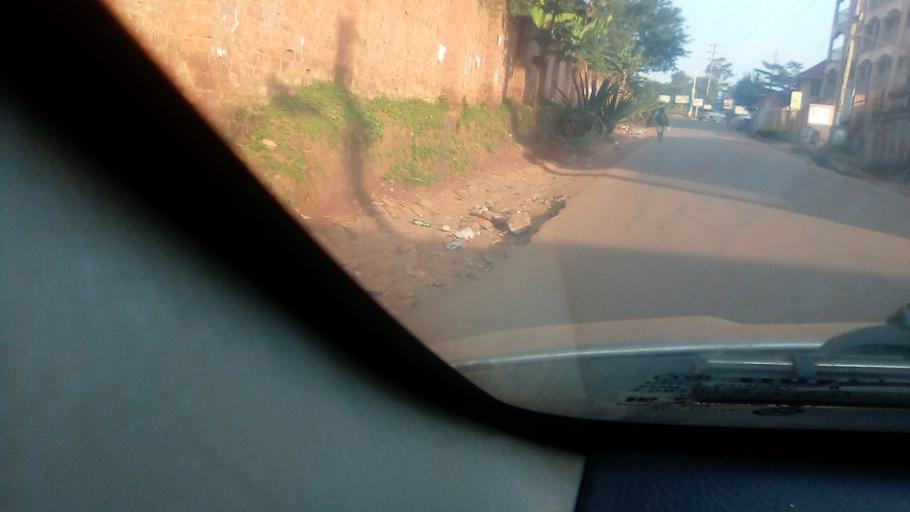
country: UG
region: Central Region
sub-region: Wakiso District
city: Kireka
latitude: 0.3449
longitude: 32.6350
